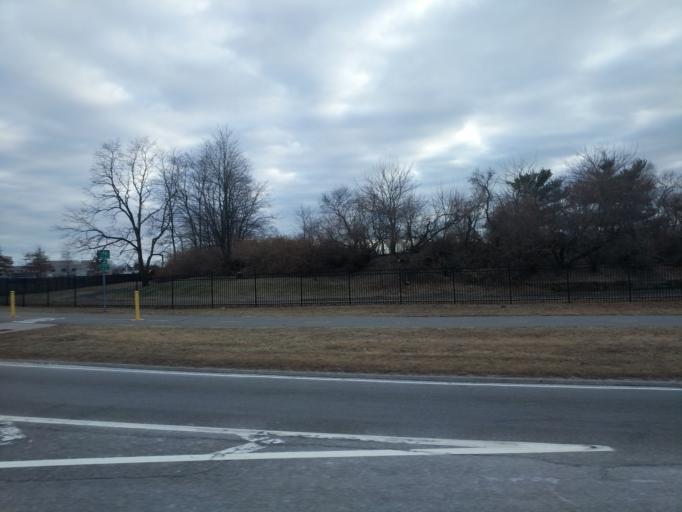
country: US
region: New York
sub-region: Nassau County
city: East Garden City
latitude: 40.7229
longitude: -73.5948
